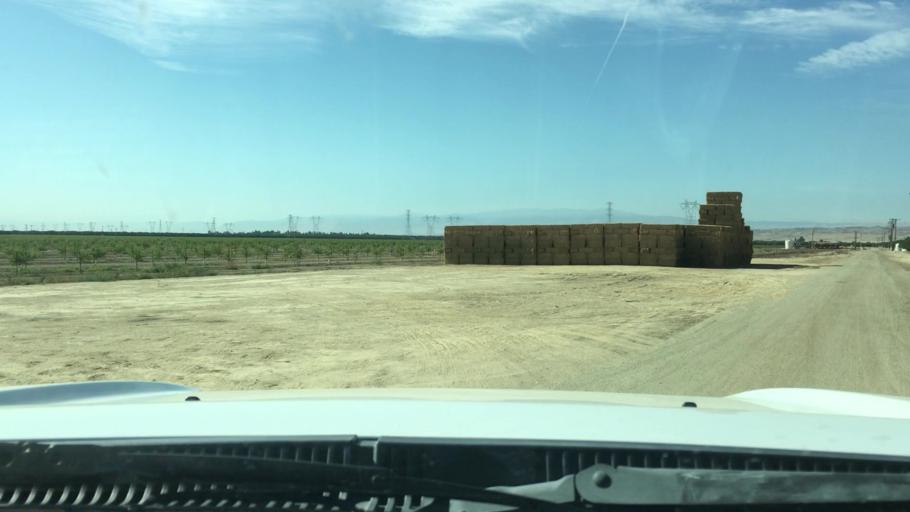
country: US
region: California
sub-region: Kern County
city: Buttonwillow
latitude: 35.3766
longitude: -119.3857
